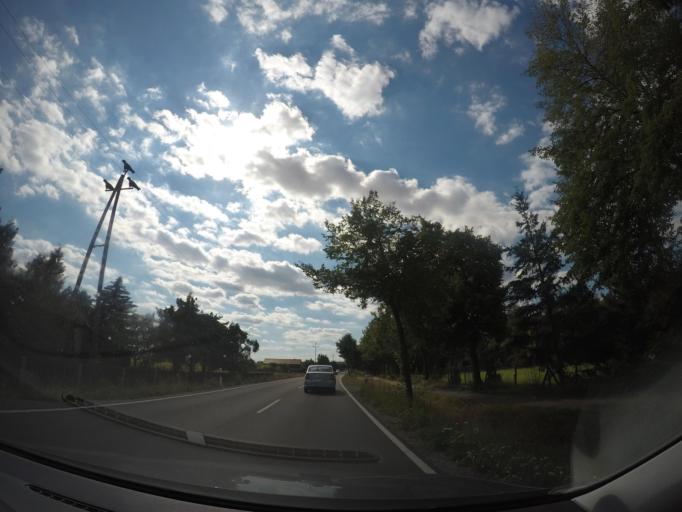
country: DE
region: Saxony-Anhalt
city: Langeln
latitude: 51.8849
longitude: 10.7700
